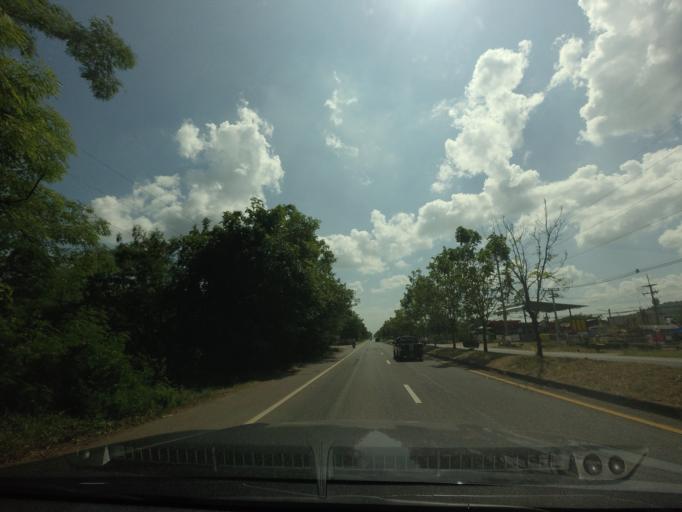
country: TH
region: Phetchabun
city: Nong Phai
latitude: 16.0266
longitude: 101.0752
